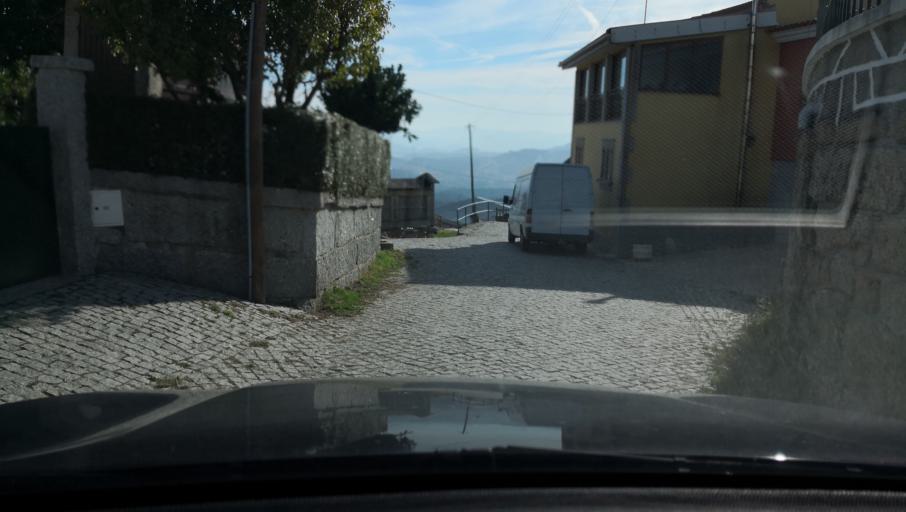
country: PT
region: Vila Real
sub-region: Vila Real
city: Vila Real
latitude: 41.3378
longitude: -7.7482
